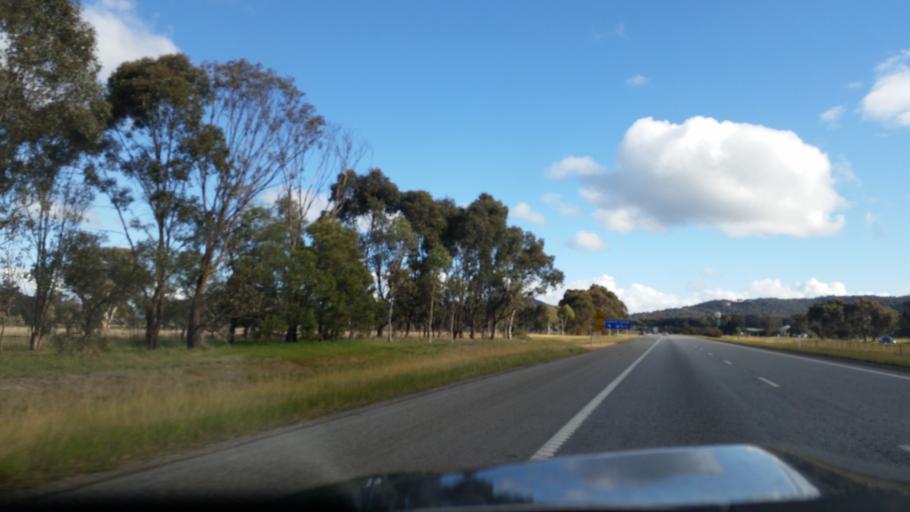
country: AU
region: Victoria
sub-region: Wangaratta
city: Wangaratta
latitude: -36.4350
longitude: 146.2534
